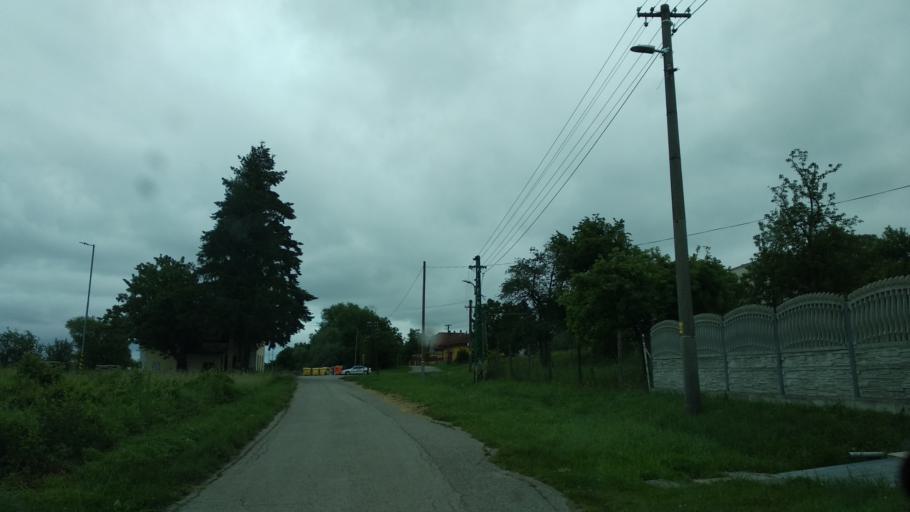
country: SK
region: Trenciansky
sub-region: Okres Trencin
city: Trencin
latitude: 48.8011
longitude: 18.1180
